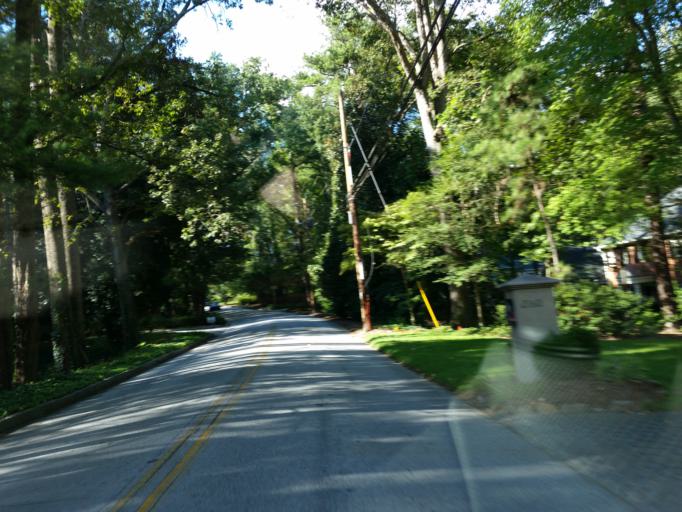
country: US
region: Georgia
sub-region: Cobb County
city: Vinings
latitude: 33.8606
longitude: -84.4391
